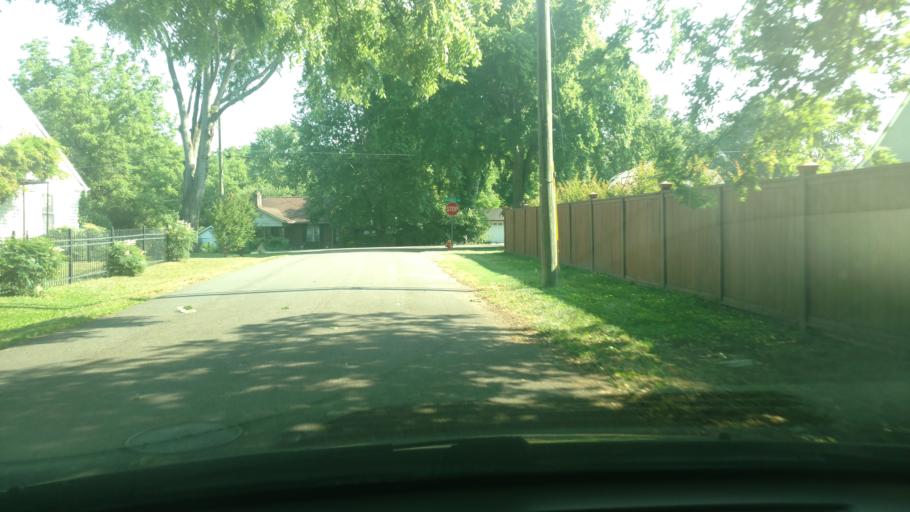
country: US
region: Tennessee
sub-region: Davidson County
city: Nashville
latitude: 36.2238
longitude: -86.7213
